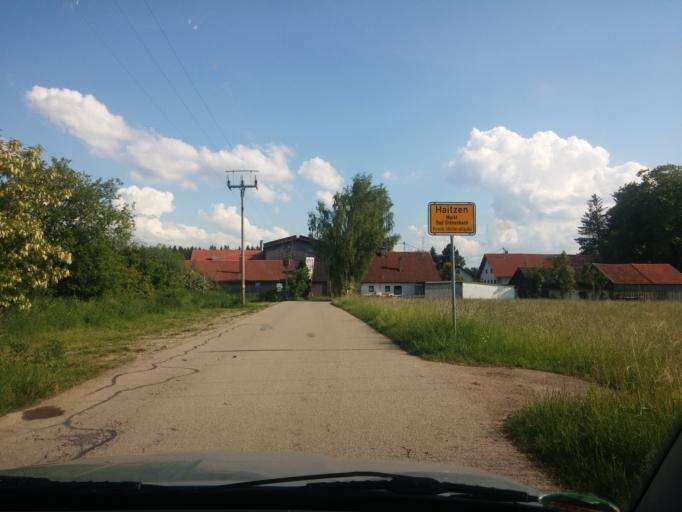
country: DE
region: Bavaria
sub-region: Swabia
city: Woringen
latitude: 47.8835
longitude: 10.1958
